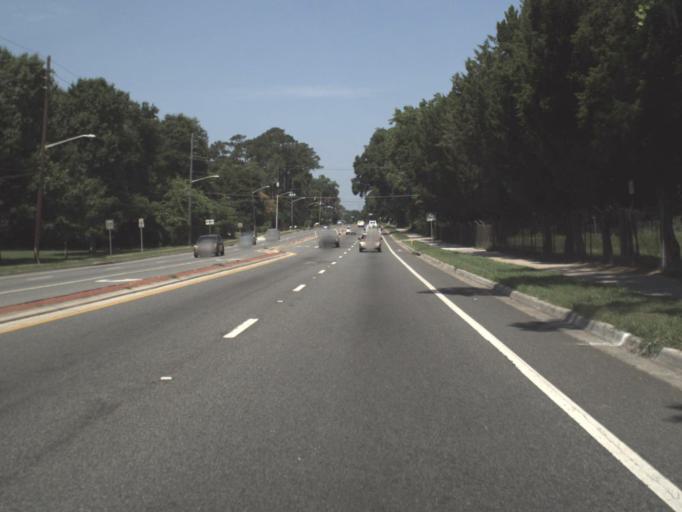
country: US
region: Florida
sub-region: Alachua County
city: Gainesville
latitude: 29.6147
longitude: -82.3433
